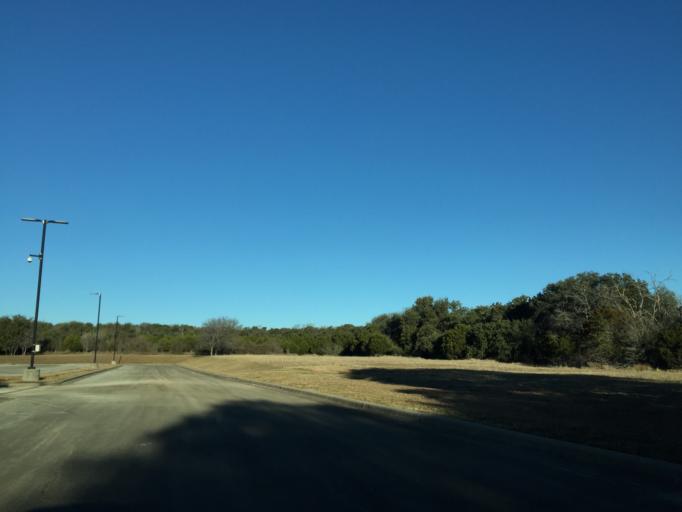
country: US
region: Texas
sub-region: Williamson County
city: Jollyville
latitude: 30.4240
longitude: -97.7443
